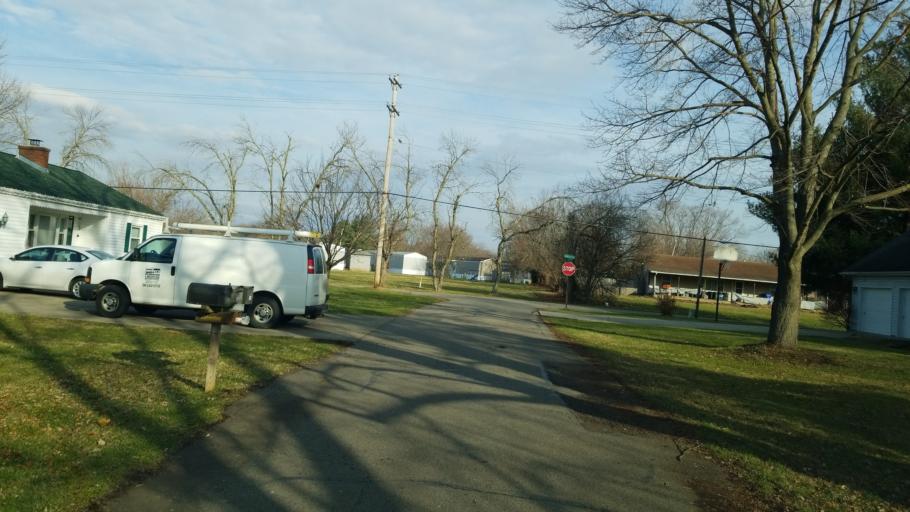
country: US
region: Ohio
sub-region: Ross County
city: Chillicothe
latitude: 39.3600
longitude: -82.9833
